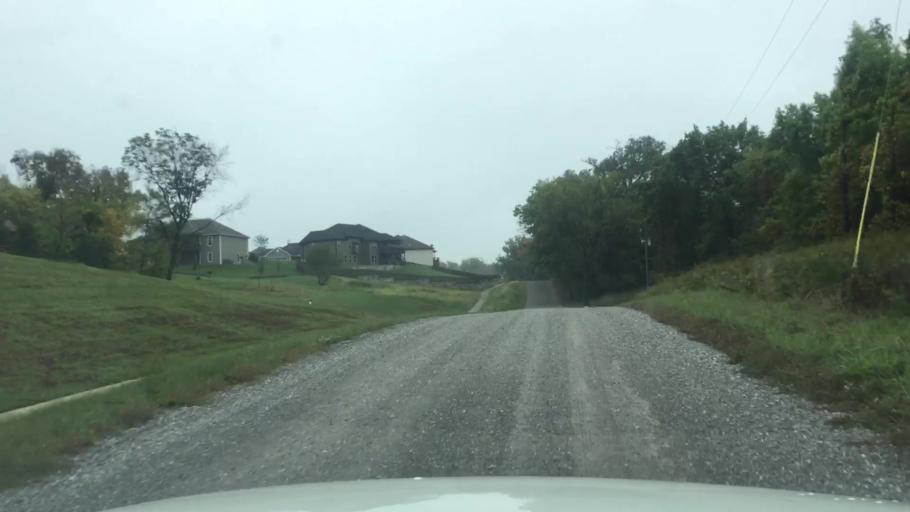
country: US
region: Missouri
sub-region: Boone County
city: Columbia
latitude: 38.8908
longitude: -92.4195
